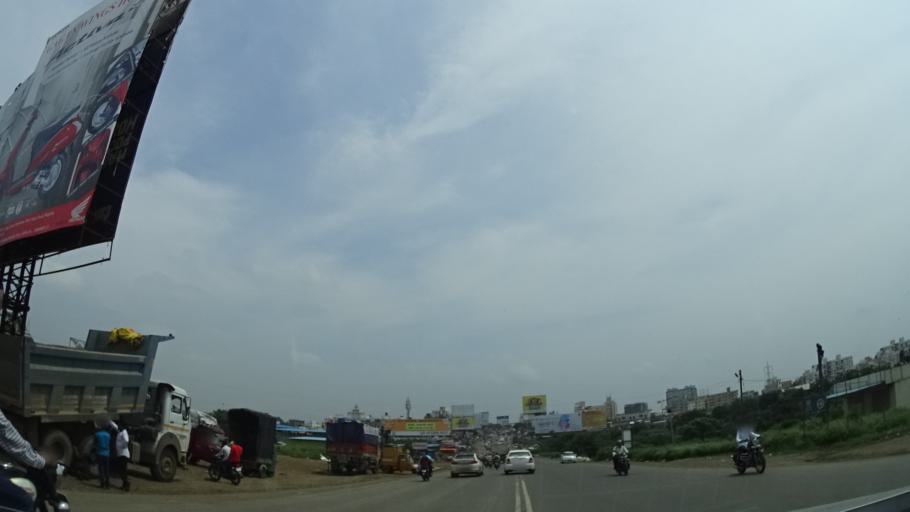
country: IN
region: Maharashtra
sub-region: Pune Division
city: Lohogaon
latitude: 18.5699
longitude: 73.9520
